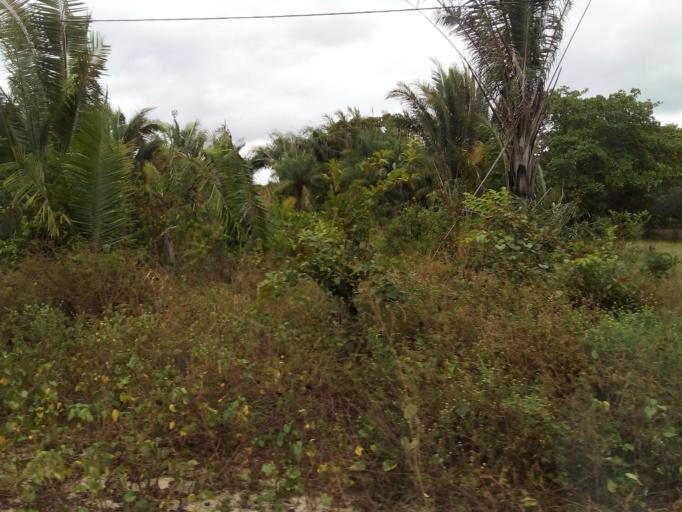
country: BR
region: Maranhao
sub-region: Sao Luis
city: Sao Luis
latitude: -2.6691
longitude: -44.2939
